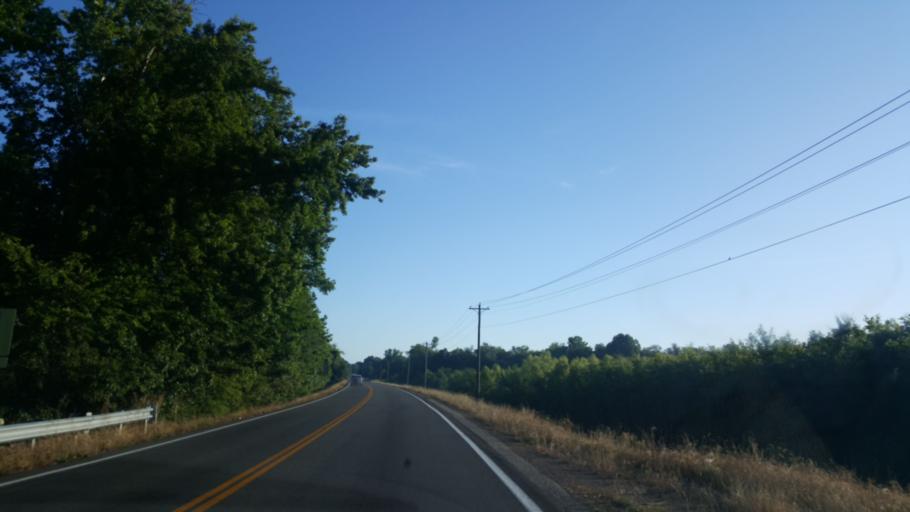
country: US
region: Tennessee
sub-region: McNairy County
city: Adamsville
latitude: 35.3593
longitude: -88.3664
